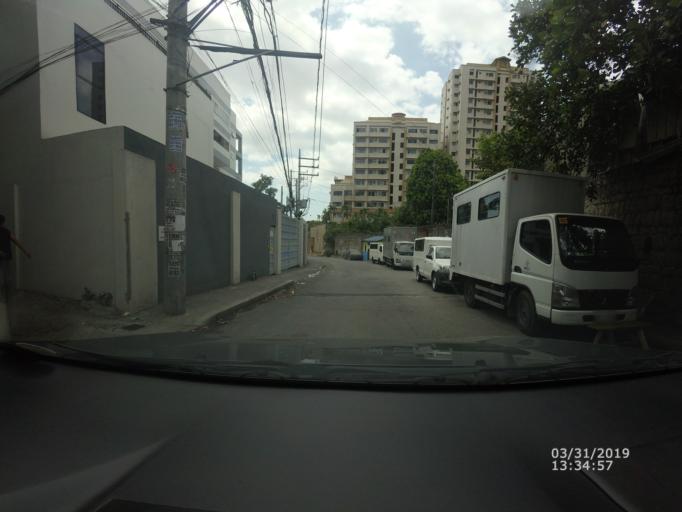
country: PH
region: Metro Manila
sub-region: Mandaluyong
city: Mandaluyong City
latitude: 14.5843
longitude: 121.0481
